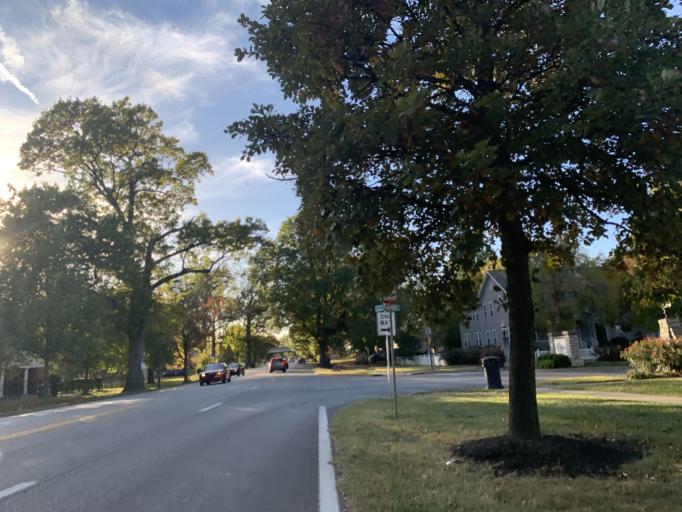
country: US
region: Kentucky
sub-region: Jefferson County
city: Shively
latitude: 38.2255
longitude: -85.8181
